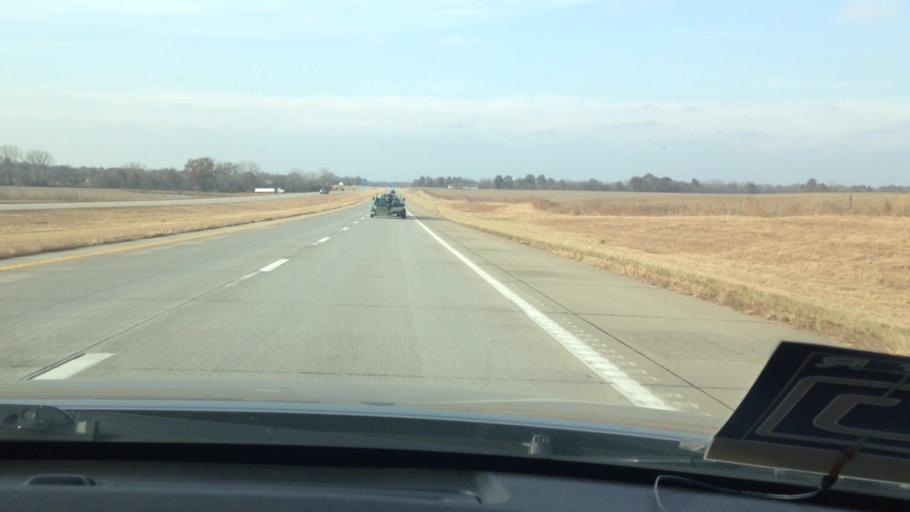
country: US
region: Missouri
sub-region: Henry County
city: Clinton
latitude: 38.4474
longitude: -93.9573
